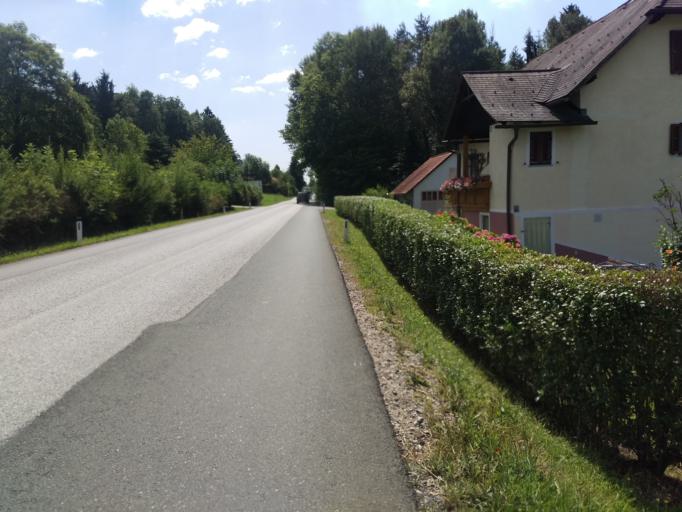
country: AT
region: Styria
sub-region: Politischer Bezirk Graz-Umgebung
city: Kumberg
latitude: 47.1480
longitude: 15.5190
